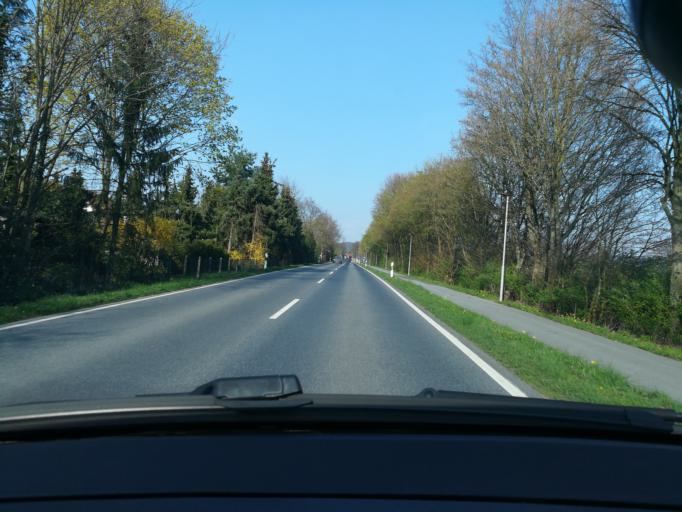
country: DE
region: North Rhine-Westphalia
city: Halle
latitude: 52.0463
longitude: 8.3443
